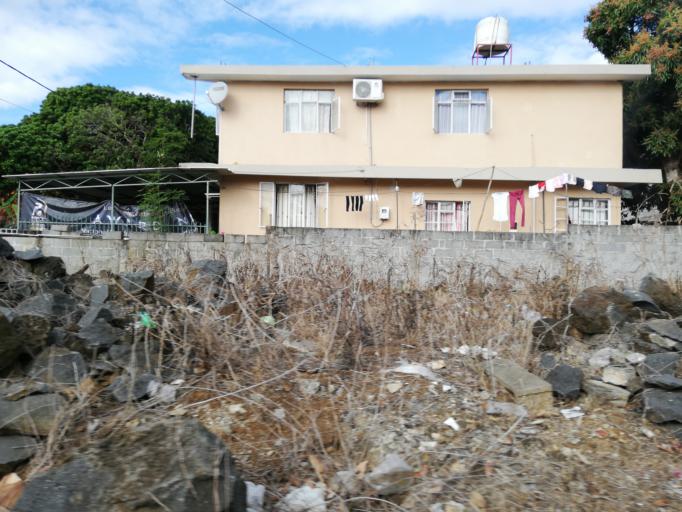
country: MU
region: Plaines Wilhems
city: Ebene
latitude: -20.2306
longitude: 57.4585
